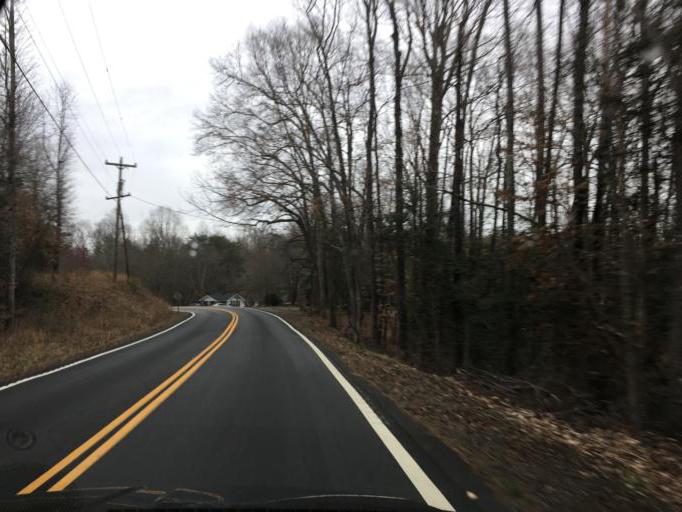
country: US
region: South Carolina
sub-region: Greenville County
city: Berea
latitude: 34.9343
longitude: -82.5113
